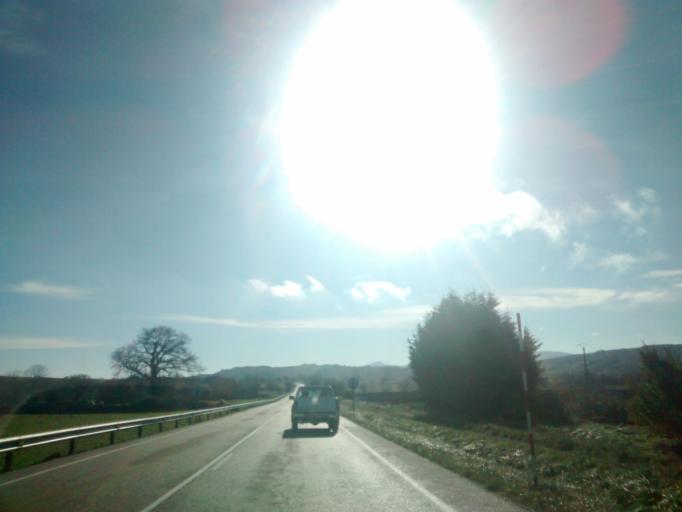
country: ES
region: Castille and Leon
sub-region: Provincia de Burgos
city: Arija
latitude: 43.0163
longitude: -3.8501
